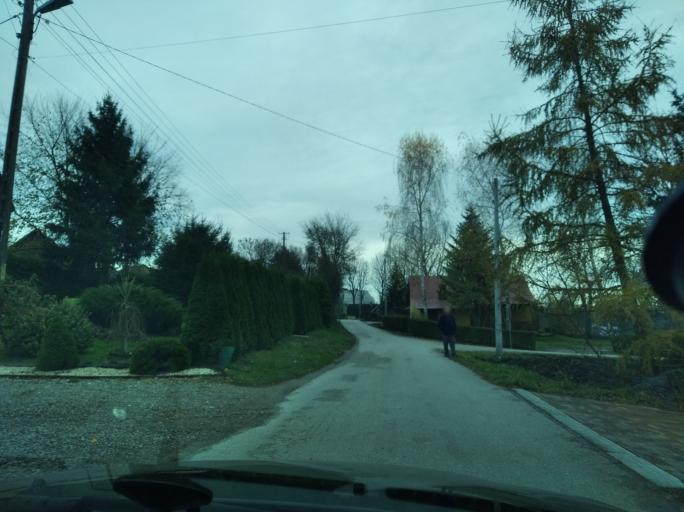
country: PL
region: Subcarpathian Voivodeship
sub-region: Powiat przeworski
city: Debow
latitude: 50.0483
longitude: 22.4357
